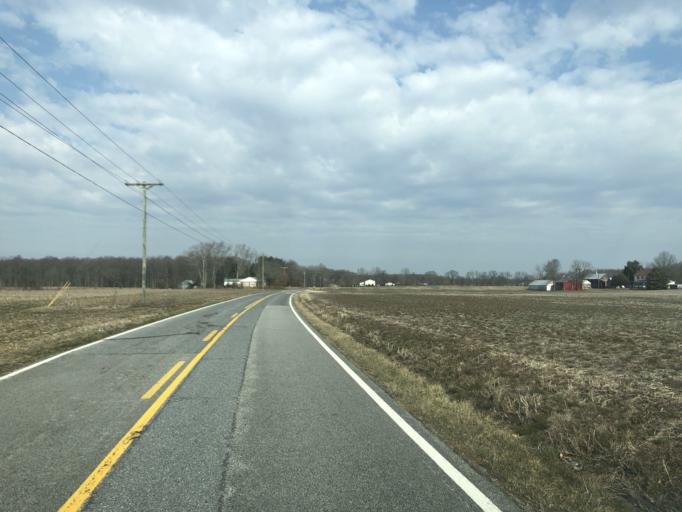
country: US
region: Maryland
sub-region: Caroline County
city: Ridgely
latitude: 39.0665
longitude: -75.9281
